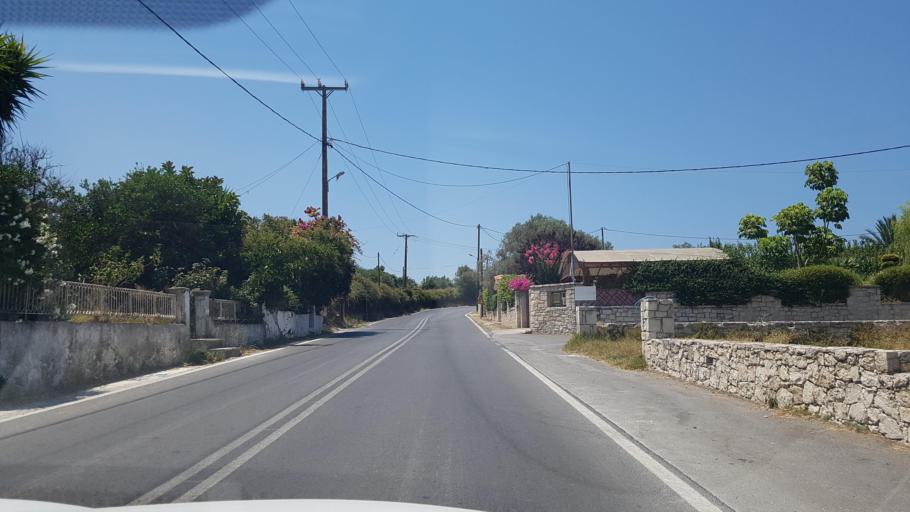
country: GR
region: Crete
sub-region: Nomos Rethymnis
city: Rethymno
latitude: 35.3570
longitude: 24.5570
